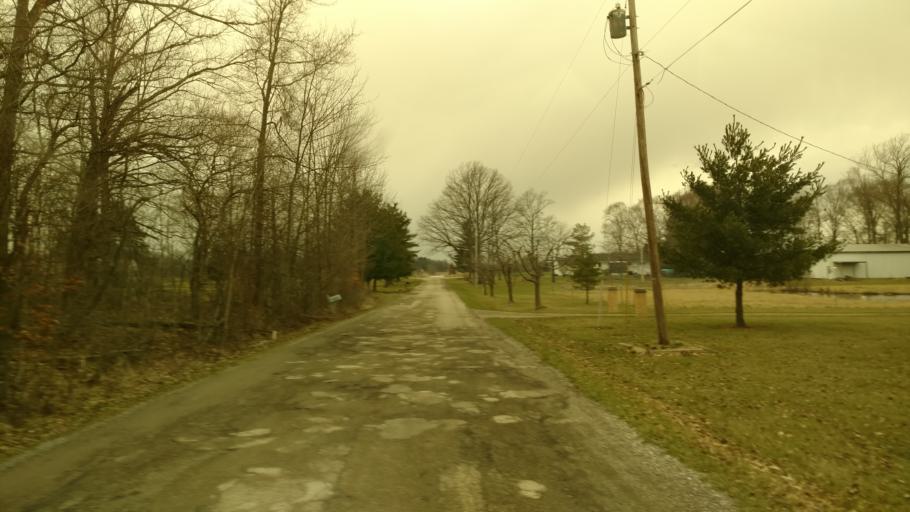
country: US
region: Ohio
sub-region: Crawford County
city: Galion
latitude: 40.6787
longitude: -82.7818
